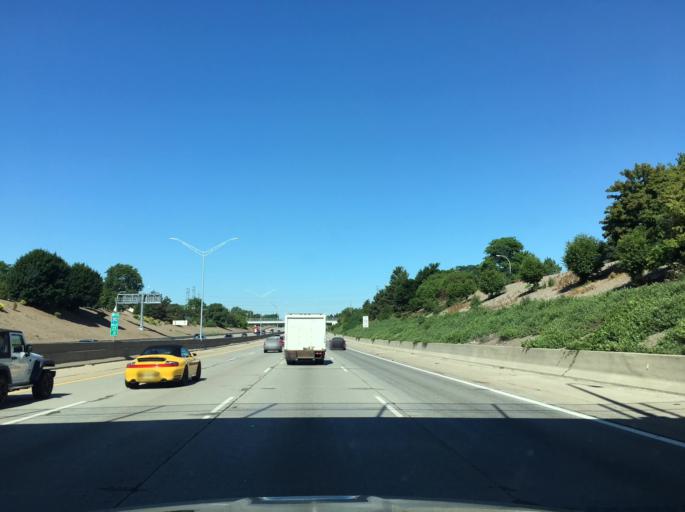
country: US
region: Michigan
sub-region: Macomb County
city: Center Line
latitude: 42.4926
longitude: -82.9889
